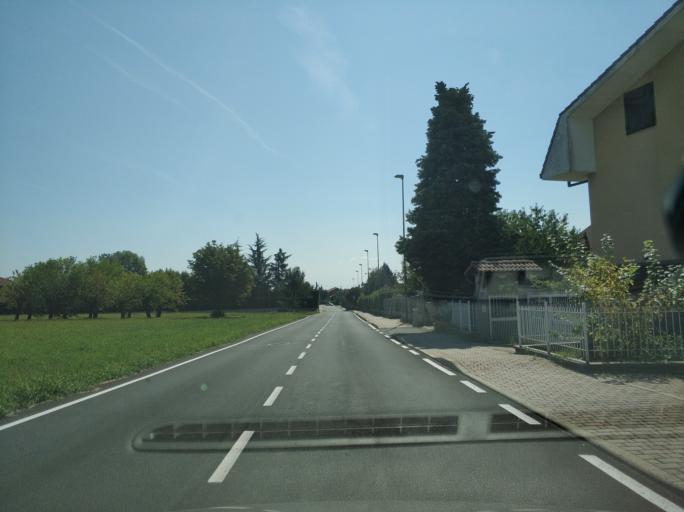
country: IT
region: Piedmont
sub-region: Provincia di Torino
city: San Francesco al Campo
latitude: 45.2339
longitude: 7.6394
